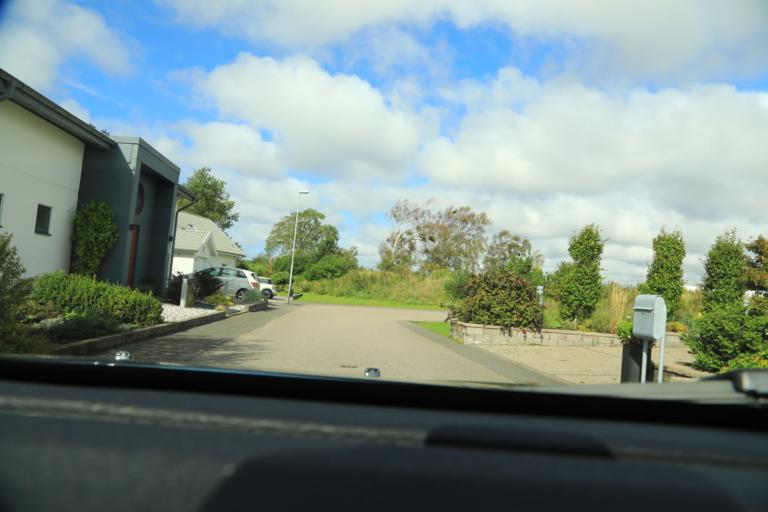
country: SE
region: Halland
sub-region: Varbergs Kommun
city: Traslovslage
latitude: 57.0808
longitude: 12.2764
